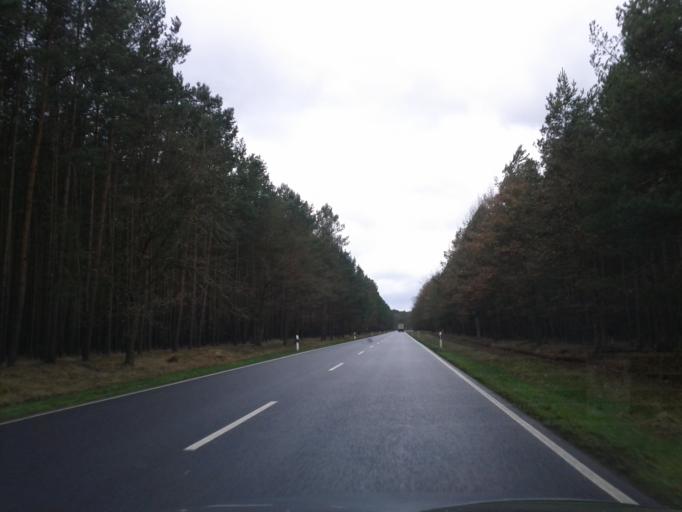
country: DE
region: Brandenburg
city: Rauen
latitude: 52.3782
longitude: 13.9878
